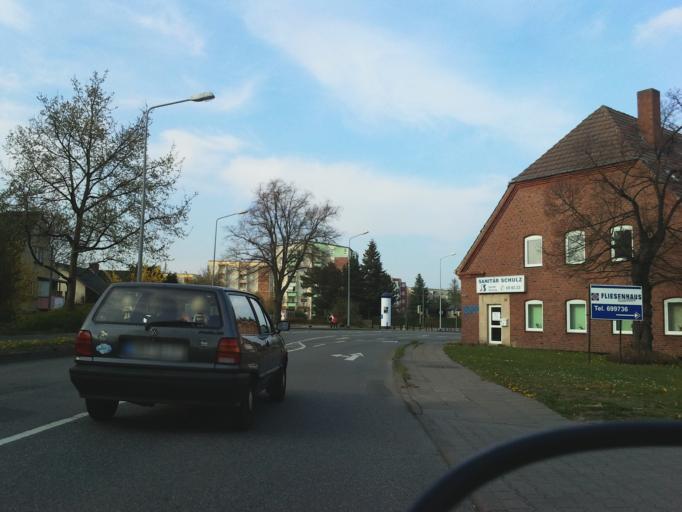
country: DE
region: Mecklenburg-Vorpommern
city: Dierkow-West
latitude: 54.1074
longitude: 12.1559
